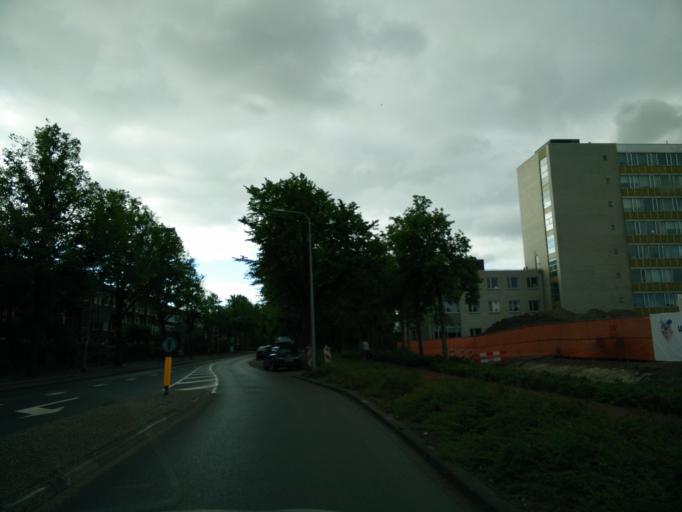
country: NL
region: Groningen
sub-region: Gemeente Groningen
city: Korrewegwijk
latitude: 53.2263
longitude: 6.5720
